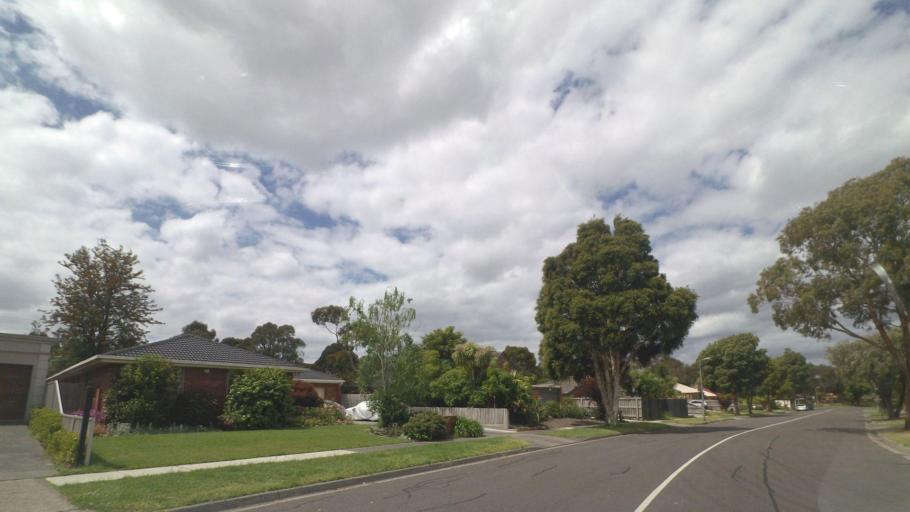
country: AU
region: Victoria
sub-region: Knox
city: Wantirna South
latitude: -37.8675
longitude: 145.2279
